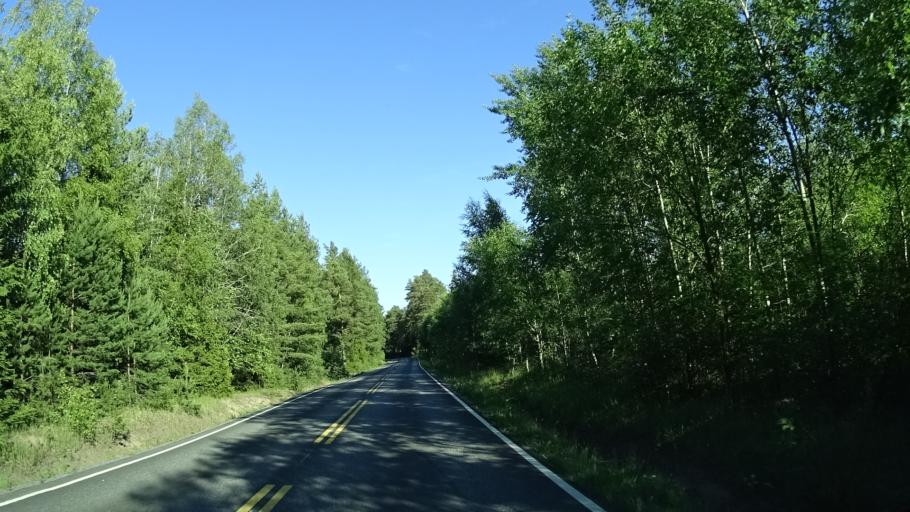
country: FI
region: Satakunta
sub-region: Pori
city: Nakkila
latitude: 61.4022
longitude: 21.9678
